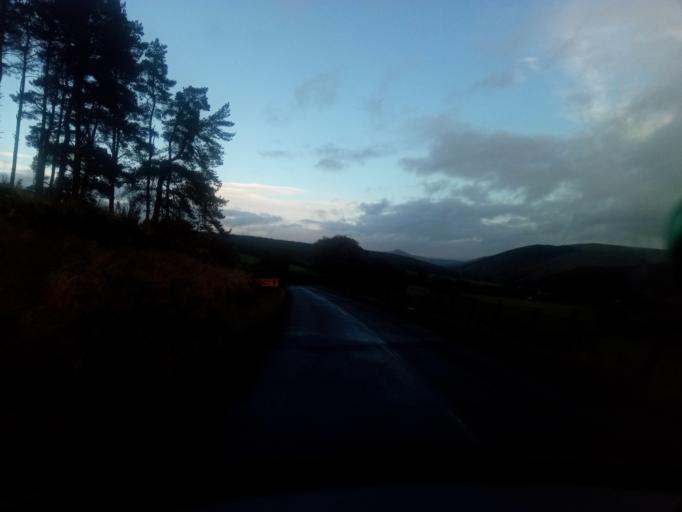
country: GB
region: Scotland
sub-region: The Scottish Borders
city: Hawick
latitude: 55.3381
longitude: -2.6514
